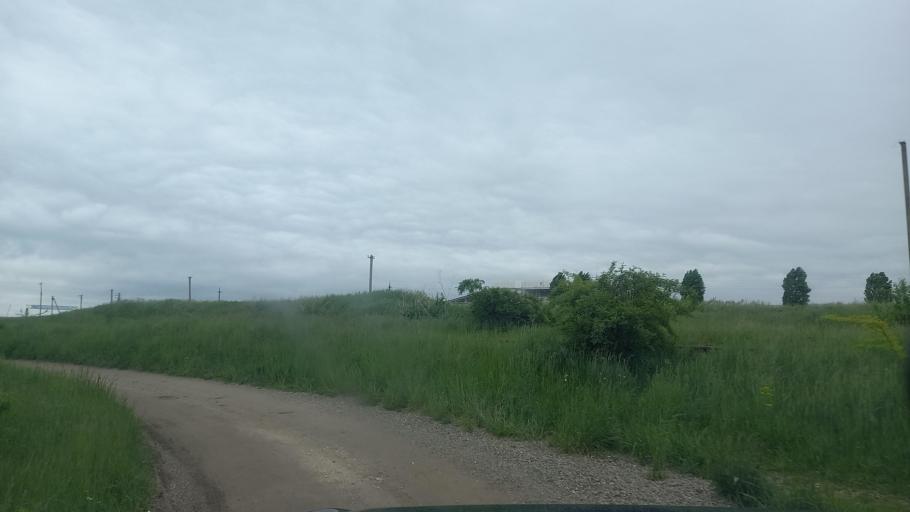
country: RU
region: Krasnodarskiy
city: Konokovo
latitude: 44.8439
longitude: 41.3484
